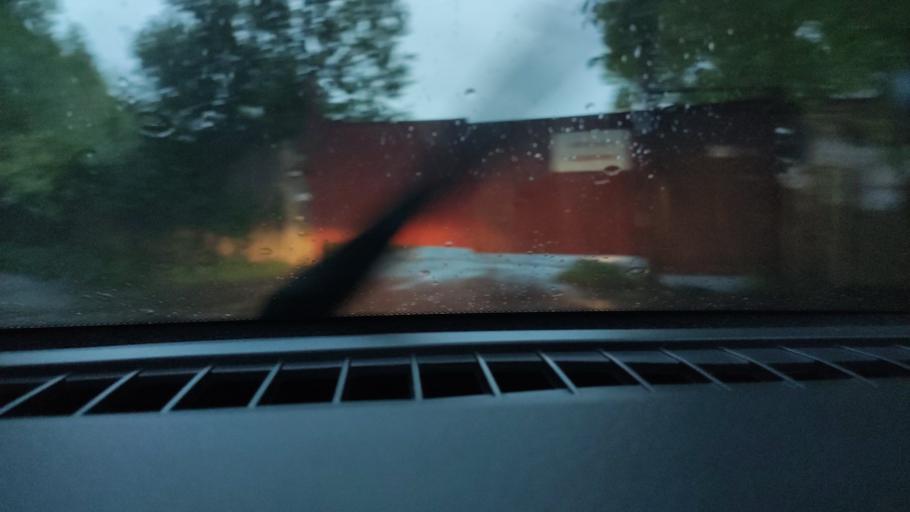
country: RU
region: Perm
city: Perm
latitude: 58.0975
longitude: 56.4152
